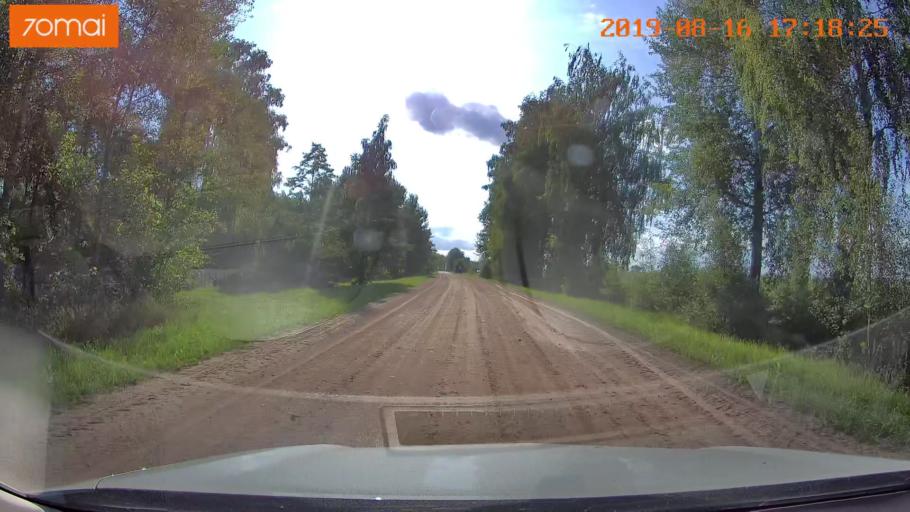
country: BY
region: Mogilev
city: Hlusha
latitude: 53.1697
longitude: 28.7890
